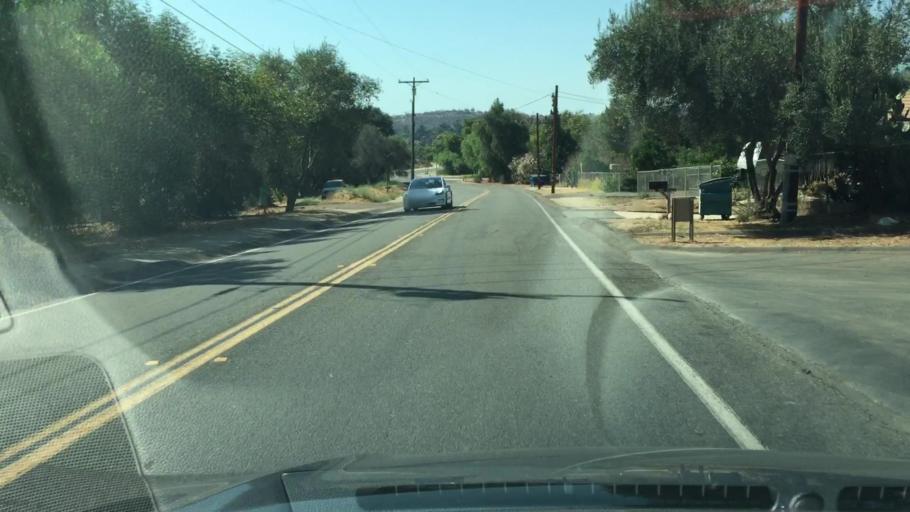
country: US
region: California
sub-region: San Diego County
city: Jamul
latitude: 32.7357
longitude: -116.8915
